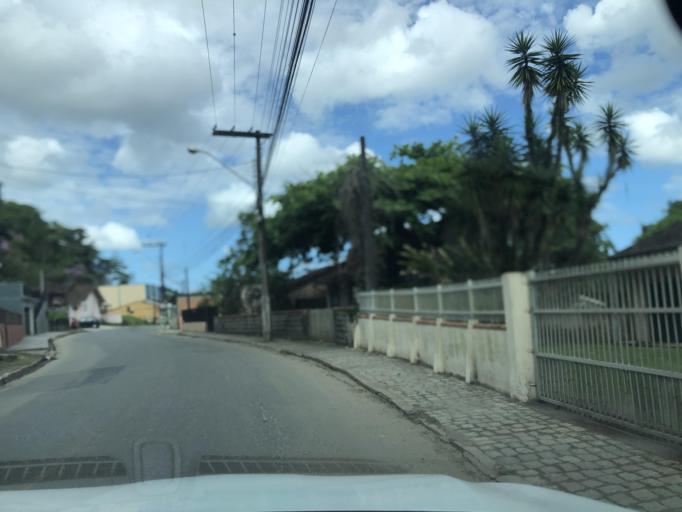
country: BR
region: Santa Catarina
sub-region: Sao Francisco Do Sul
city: Sao Francisco do Sul
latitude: -26.2441
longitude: -48.6330
